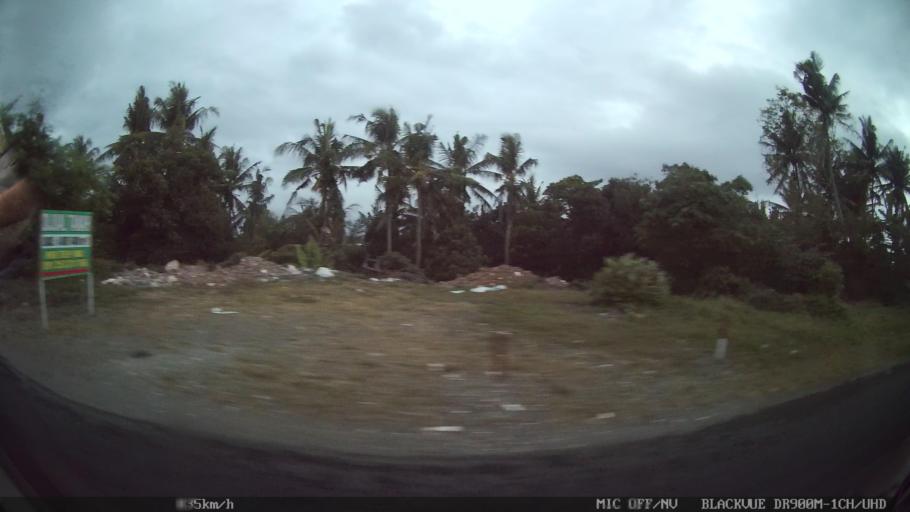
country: ID
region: Bali
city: Banjar Pasekan
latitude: -8.6137
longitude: 115.2948
